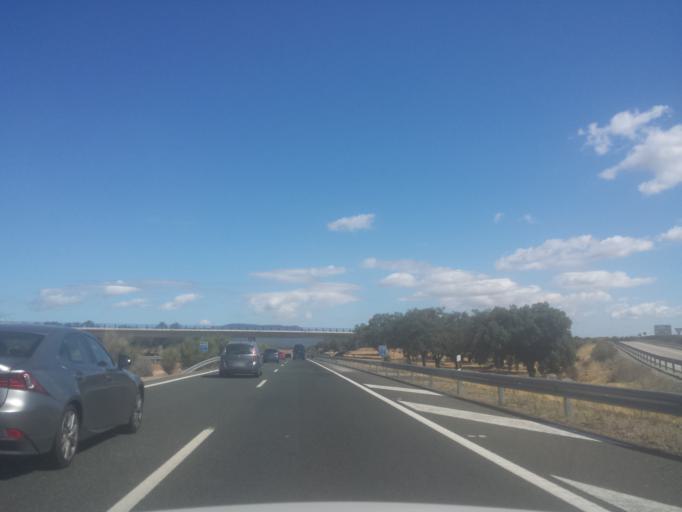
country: ES
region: Andalusia
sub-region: Provincia de Huelva
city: Santa Olalla del Cala
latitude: 37.9489
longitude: -6.2296
